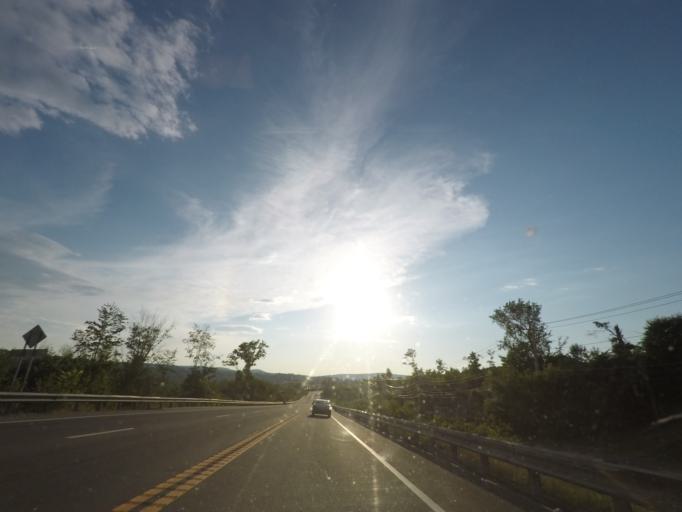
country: US
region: Massachusetts
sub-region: Hampden County
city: Brimfield
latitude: 42.1092
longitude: -72.1731
